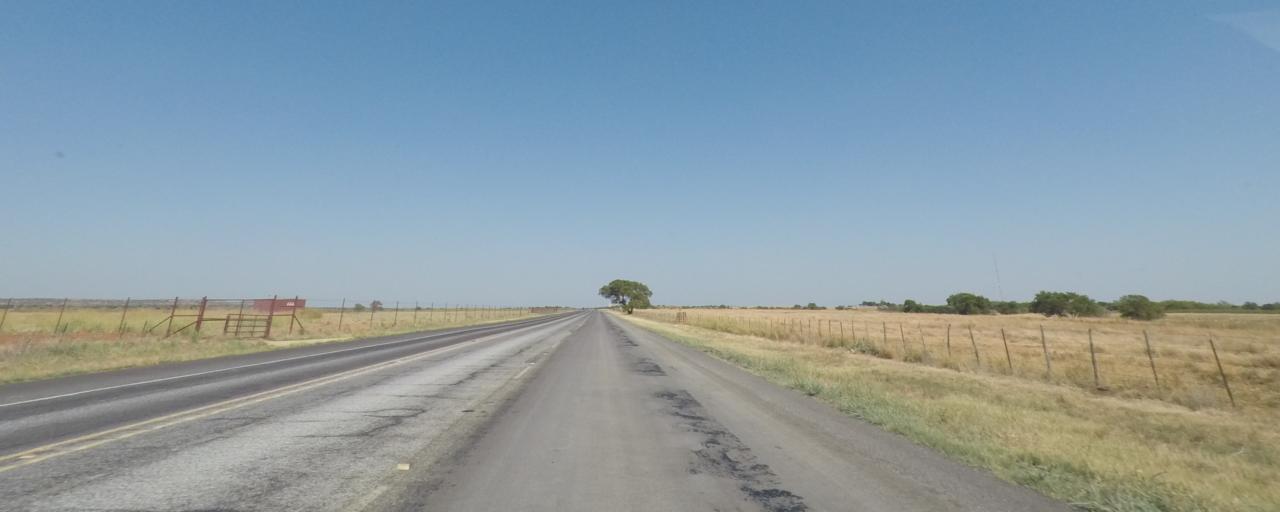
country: US
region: Texas
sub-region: King County
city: Guthrie
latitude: 33.6328
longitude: -100.3527
